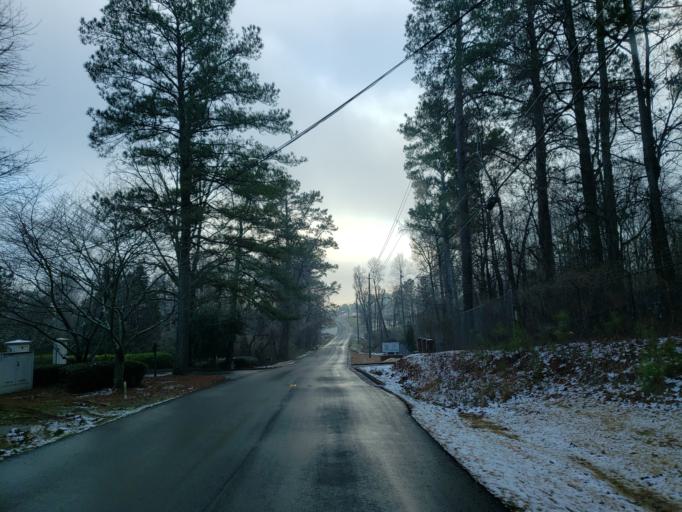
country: US
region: Georgia
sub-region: Cobb County
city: Kennesaw
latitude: 34.0265
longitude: -84.5914
